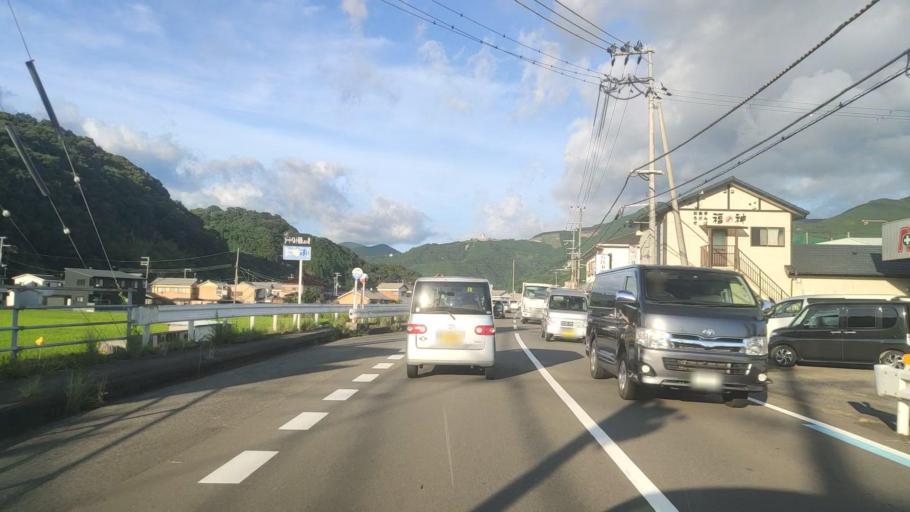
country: JP
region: Wakayama
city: Tanabe
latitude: 33.7159
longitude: 135.4609
